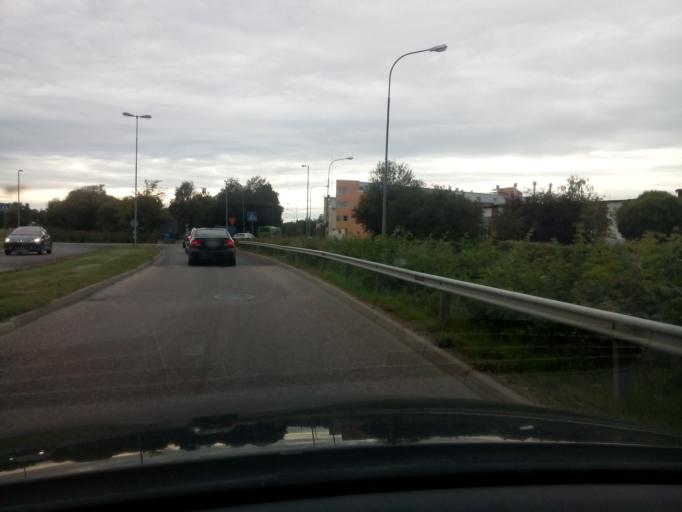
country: SE
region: Soedermanland
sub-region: Nykopings Kommun
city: Nykoping
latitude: 58.7472
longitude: 17.0075
